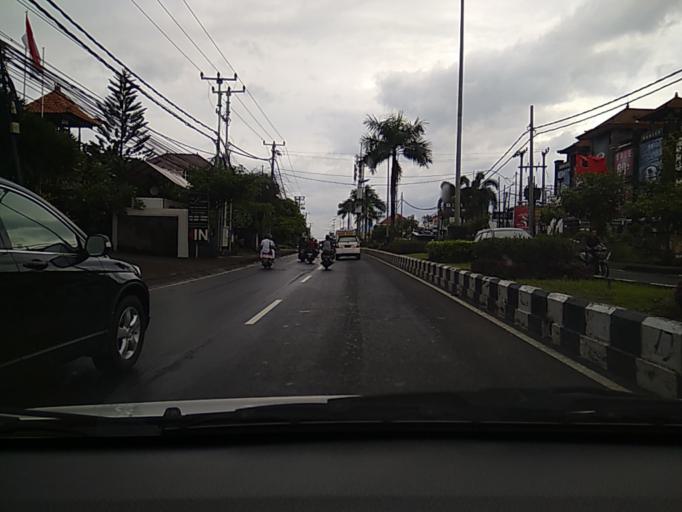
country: ID
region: Bali
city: Bualu
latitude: -8.7857
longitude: 115.2020
